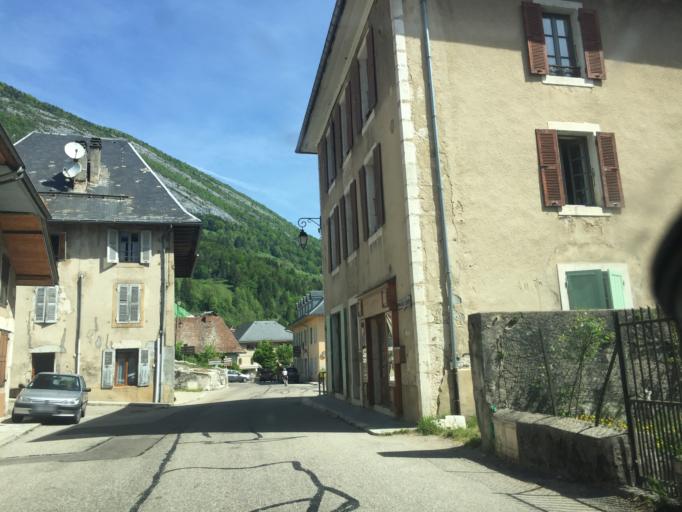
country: FR
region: Rhone-Alpes
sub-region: Departement de la Savoie
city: Les Echelles
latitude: 45.4145
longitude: 5.8546
